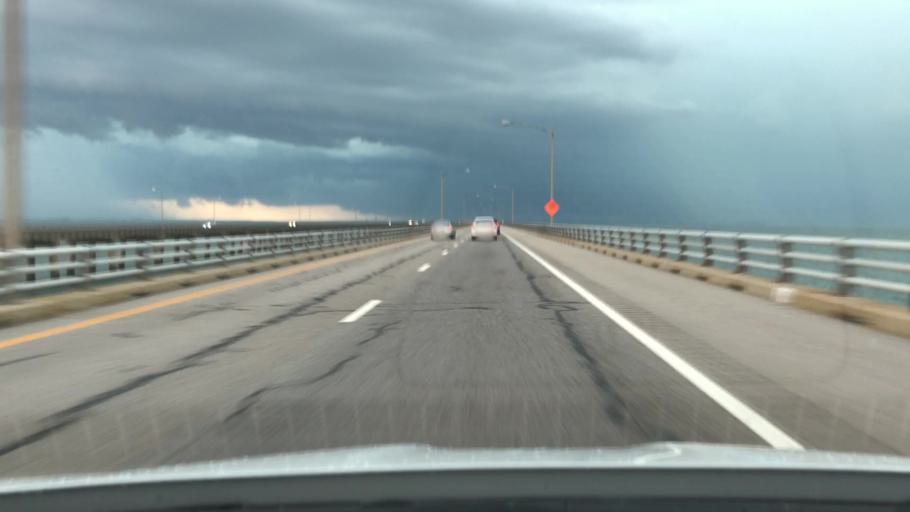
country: US
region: Virginia
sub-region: City of Virginia Beach
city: Virginia Beach
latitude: 37.0064
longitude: -76.0970
